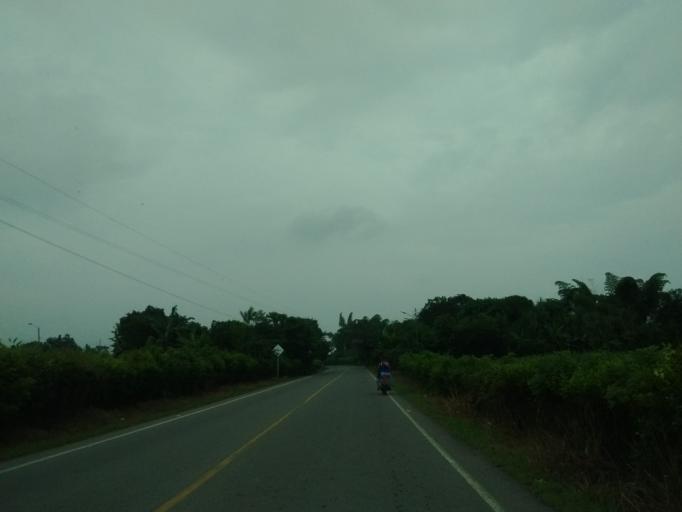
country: CO
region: Cauca
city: Padilla
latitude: 3.2293
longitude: -76.3227
